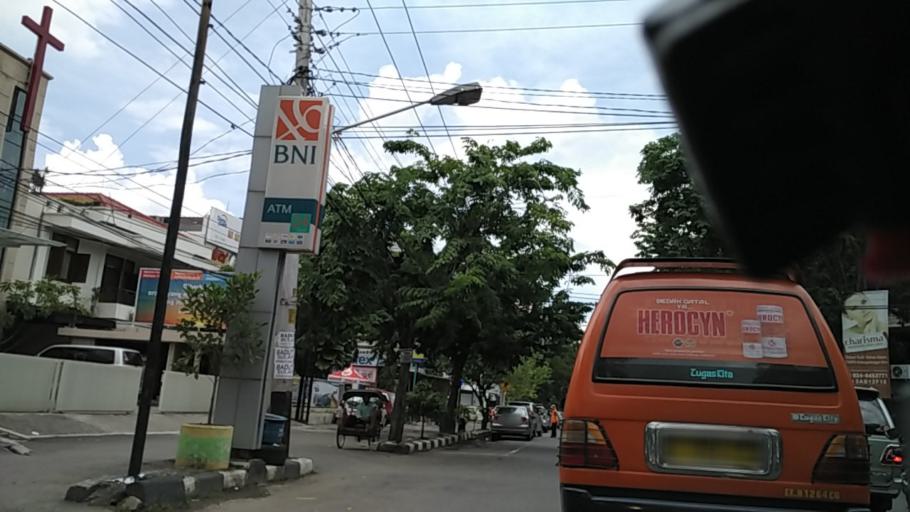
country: ID
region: Central Java
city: Semarang
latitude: -6.9894
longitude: 110.4318
